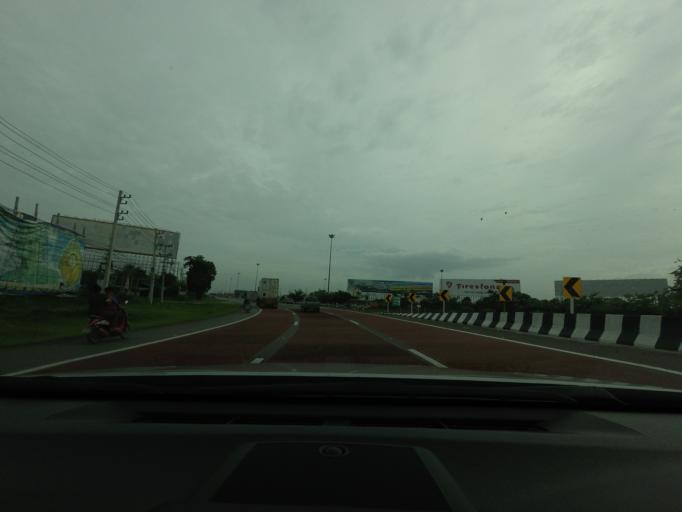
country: TH
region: Ratchaburi
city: Pak Tho
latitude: 13.3395
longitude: 99.8316
